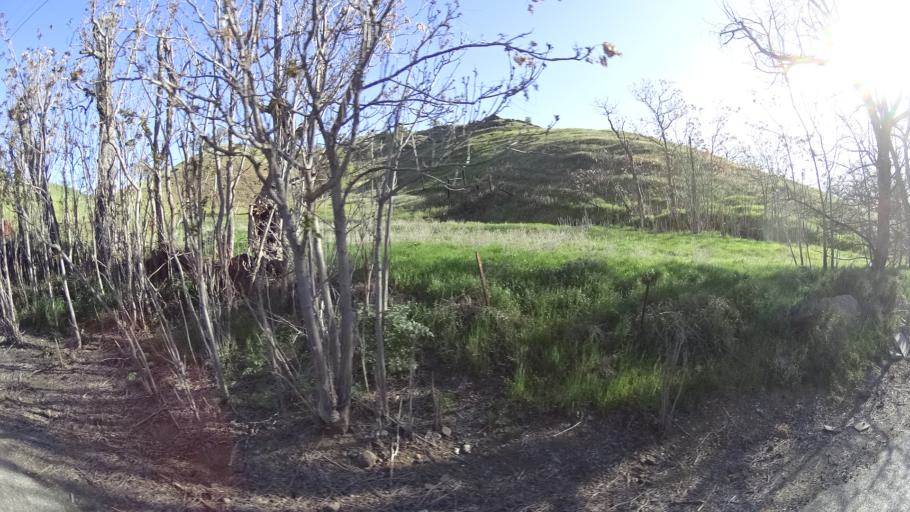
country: US
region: California
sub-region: Tehama County
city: Rancho Tehama Reserve
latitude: 39.7926
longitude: -122.5273
